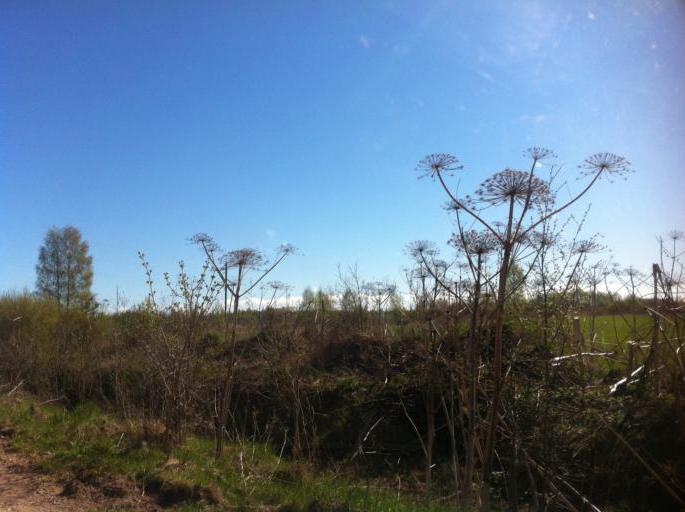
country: RU
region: Pskov
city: Izborsk
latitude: 57.8069
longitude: 27.9763
